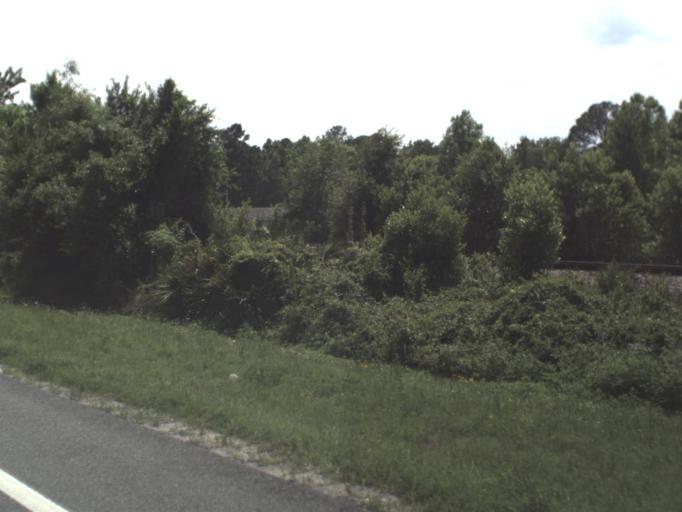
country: US
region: Florida
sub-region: Nassau County
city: Yulee
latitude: 30.4850
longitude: -81.6268
